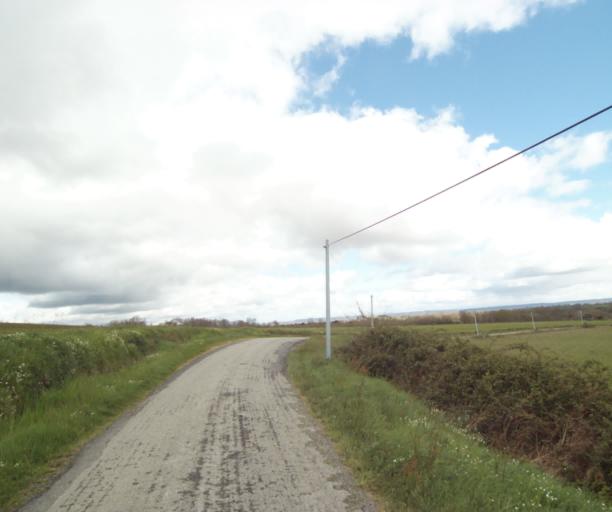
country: FR
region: Midi-Pyrenees
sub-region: Departement de l'Ariege
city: Saverdun
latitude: 43.2086
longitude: 1.5670
